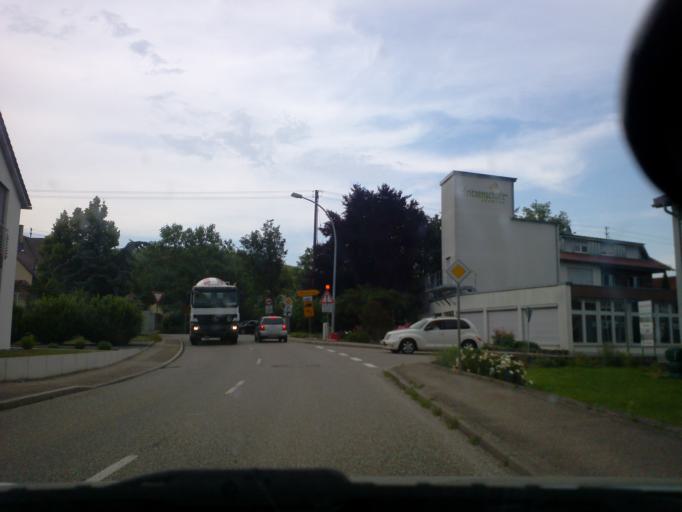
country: DE
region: Baden-Wuerttemberg
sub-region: Regierungsbezirk Stuttgart
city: Guglingen
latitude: 49.0840
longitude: 9.0184
